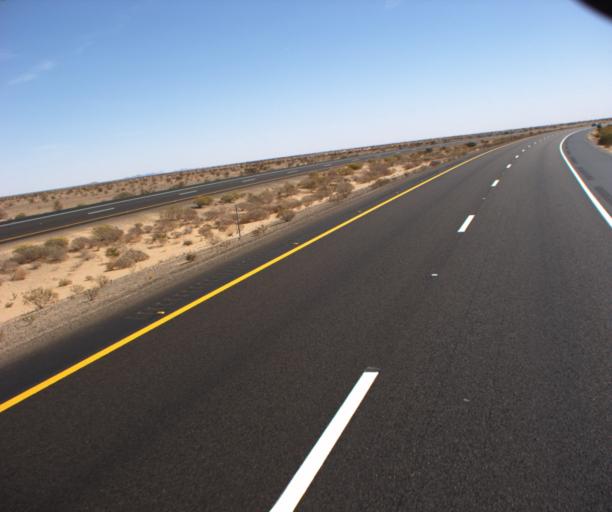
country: US
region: Arizona
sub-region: Yuma County
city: Somerton
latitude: 32.5061
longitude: -114.5584
